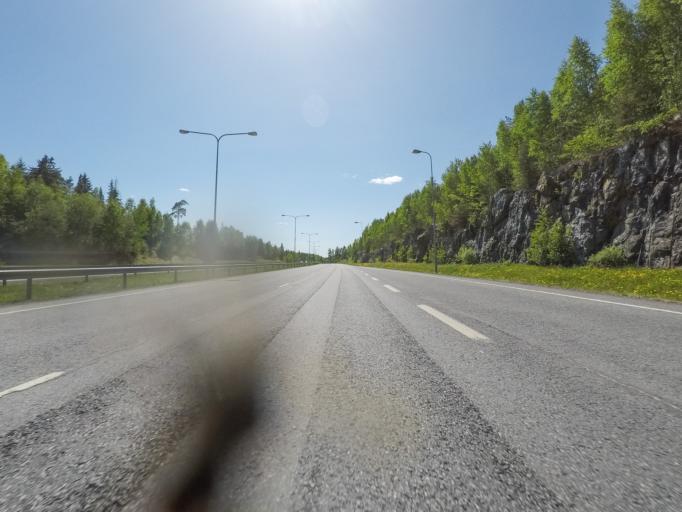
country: FI
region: Pirkanmaa
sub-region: Etelae-Pirkanmaa
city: Toijala
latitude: 61.1946
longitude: 23.8139
